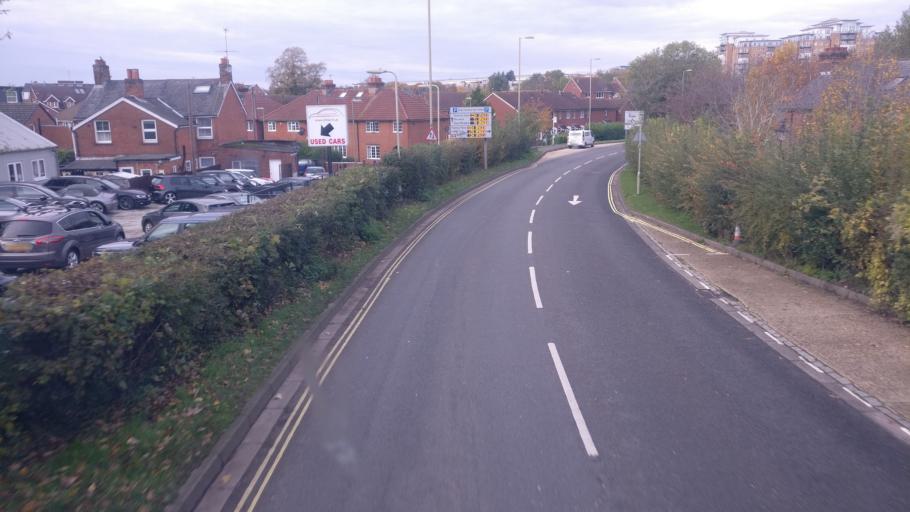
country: GB
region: England
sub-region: Hampshire
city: Basingstoke
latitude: 51.2642
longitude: -1.0908
